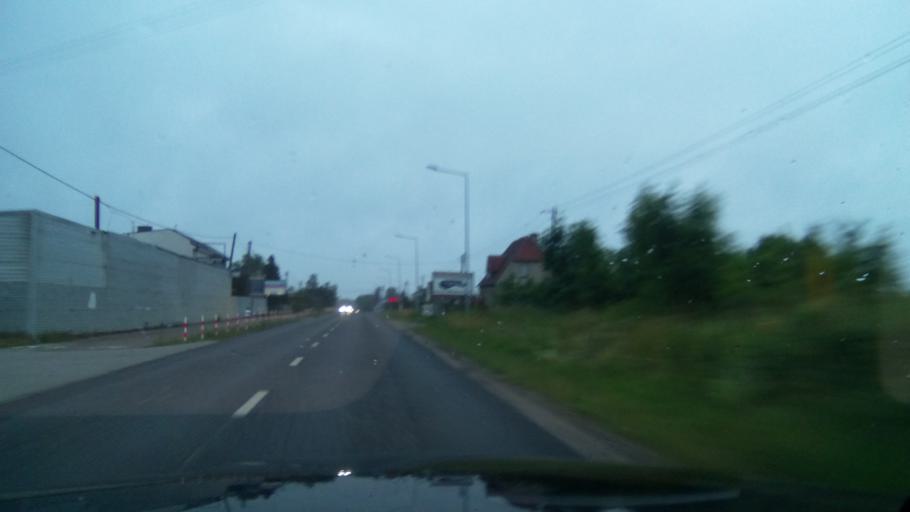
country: PL
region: Greater Poland Voivodeship
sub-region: Powiat poznanski
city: Kobylnica
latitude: 52.4341
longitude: 17.0733
